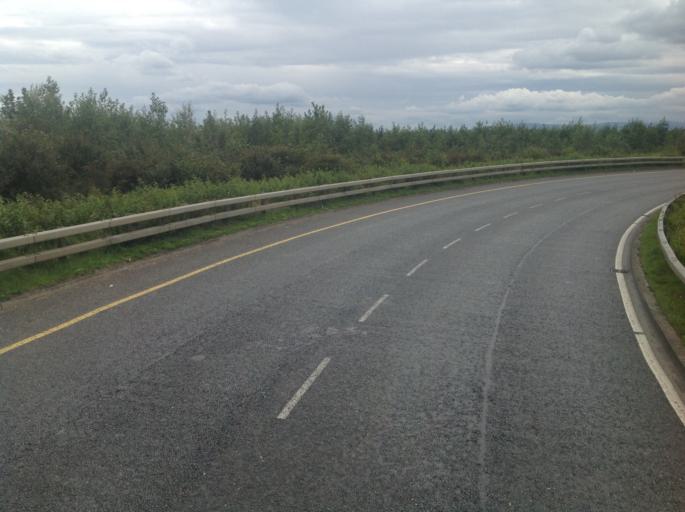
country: IE
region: Leinster
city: Kinsealy-Drinan
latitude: 53.4272
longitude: -6.2160
